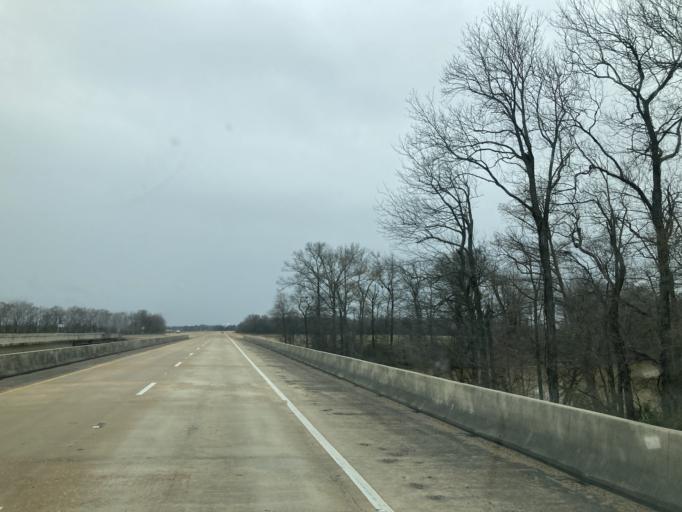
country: US
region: Mississippi
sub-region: Humphreys County
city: Belzoni
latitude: 33.0761
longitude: -90.4776
